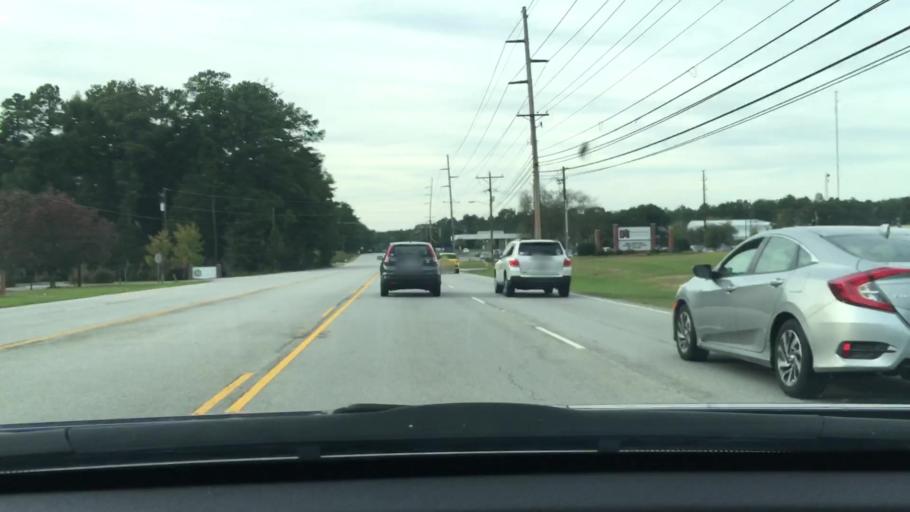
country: US
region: South Carolina
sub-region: Lexington County
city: Saint Andrews
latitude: 34.0740
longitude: -81.1236
